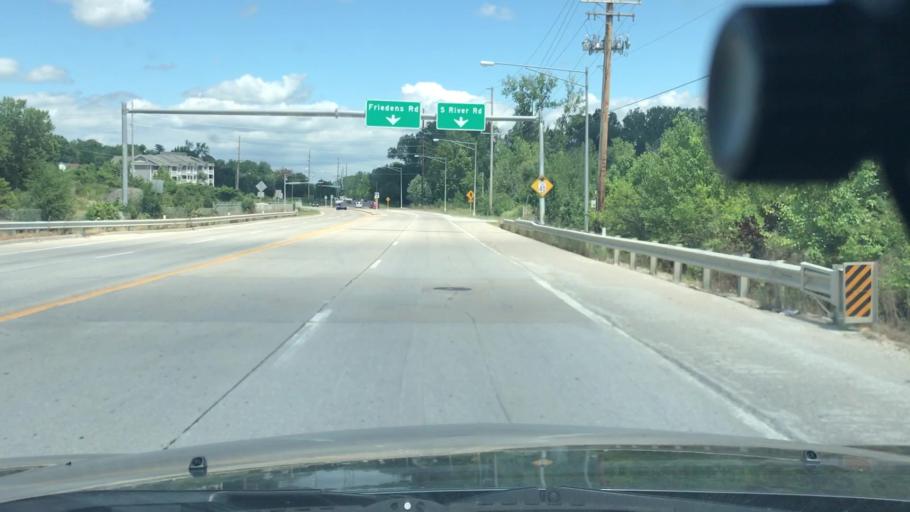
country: US
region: Missouri
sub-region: Saint Charles County
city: Saint Charles
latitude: 38.7533
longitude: -90.5032
